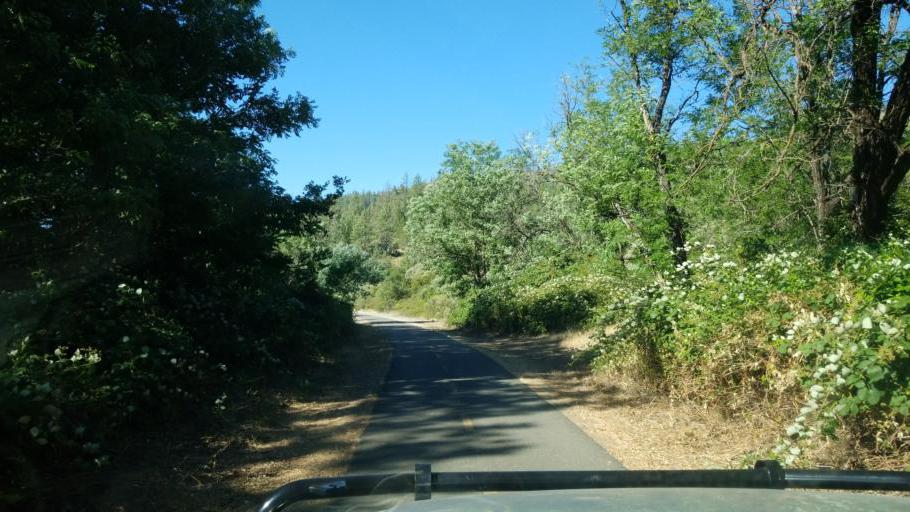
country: US
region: California
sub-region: Shasta County
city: Shasta
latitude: 40.6747
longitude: -122.4603
